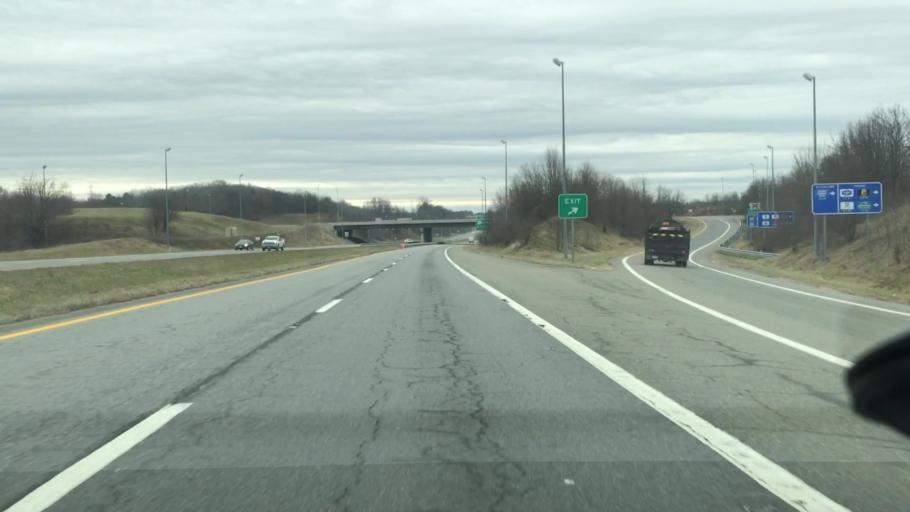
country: US
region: Virginia
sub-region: Montgomery County
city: Merrimac
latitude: 37.1674
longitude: -80.4158
